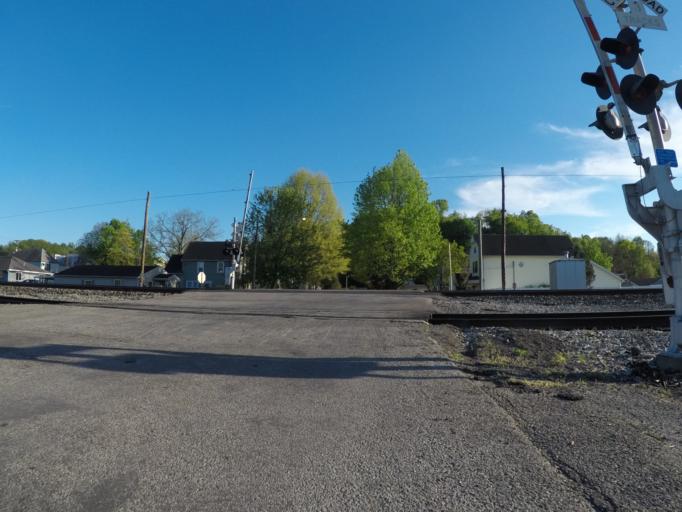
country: US
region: West Virginia
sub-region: Wayne County
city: Ceredo
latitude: 38.3928
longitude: -82.5606
